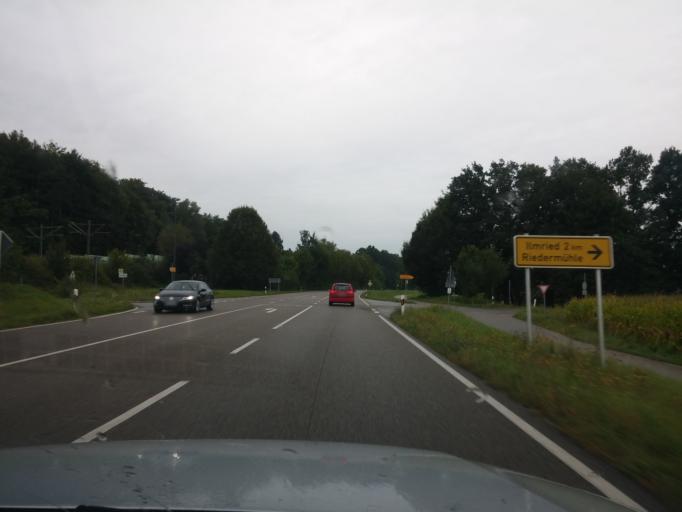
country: DE
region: Bavaria
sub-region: Upper Bavaria
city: Ilmmunster
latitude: 48.4767
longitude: 11.5095
